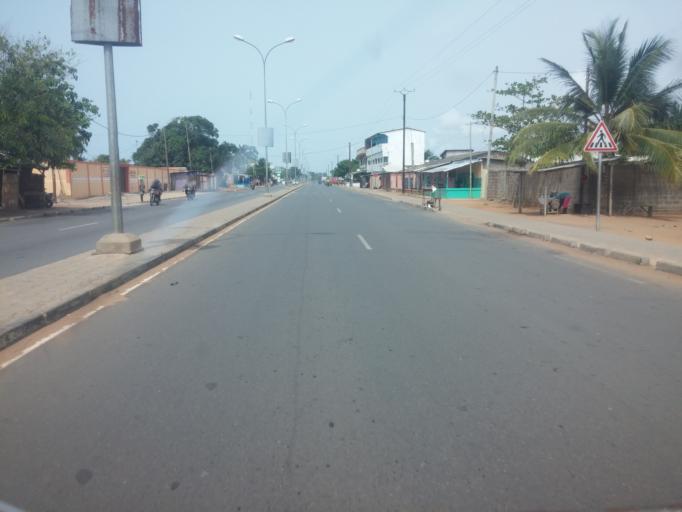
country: TG
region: Maritime
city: Aneho
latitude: 6.2400
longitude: 1.6226
